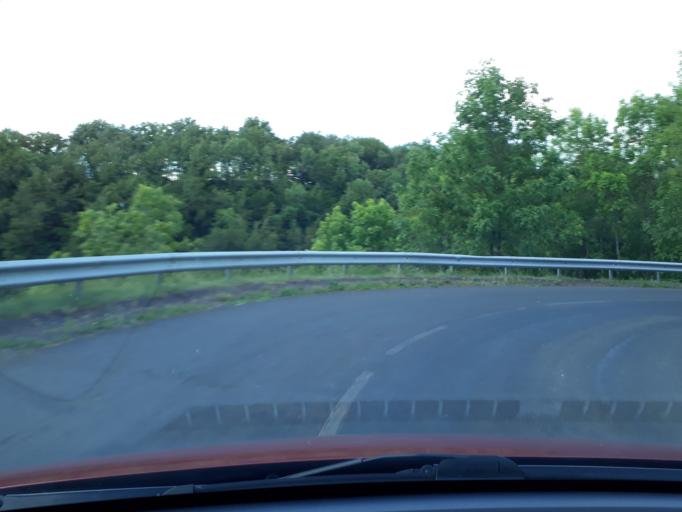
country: FR
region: Languedoc-Roussillon
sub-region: Departement de la Lozere
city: Langogne
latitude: 44.8166
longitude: 3.9334
